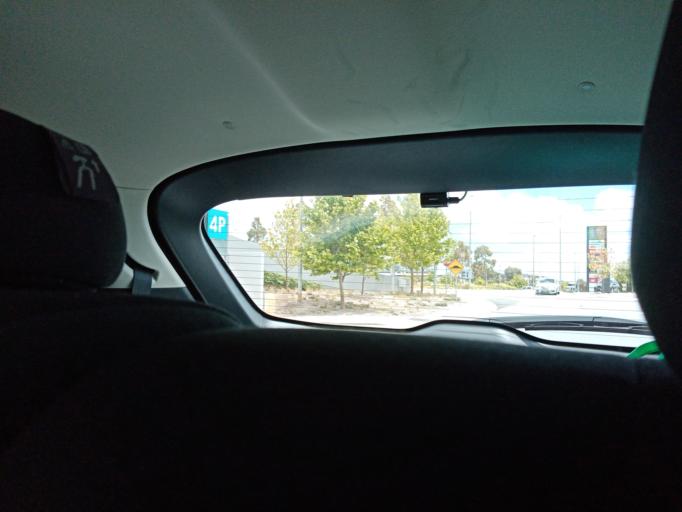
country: AU
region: Western Australia
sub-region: City of Cockburn
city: Success
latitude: -32.1296
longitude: 115.8581
